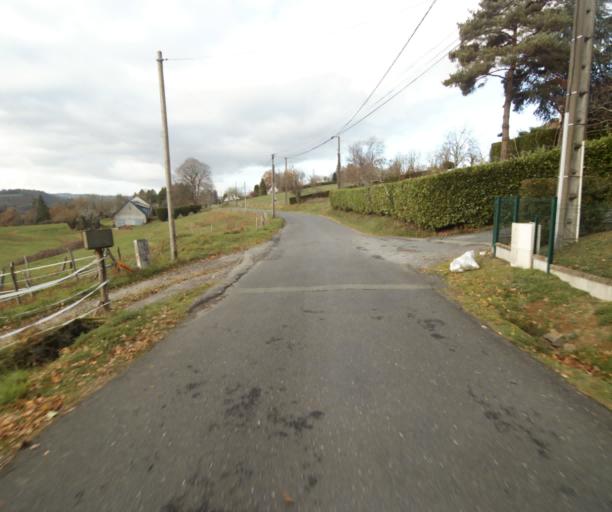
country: FR
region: Limousin
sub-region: Departement de la Correze
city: Laguenne
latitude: 45.2317
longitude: 1.7912
